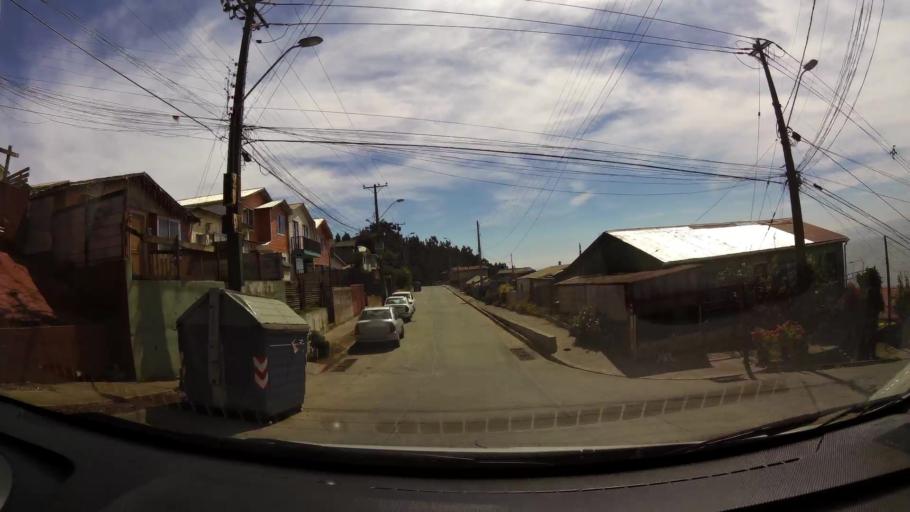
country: CL
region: Biobio
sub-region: Provincia de Concepcion
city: Talcahuano
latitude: -36.7090
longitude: -73.1191
